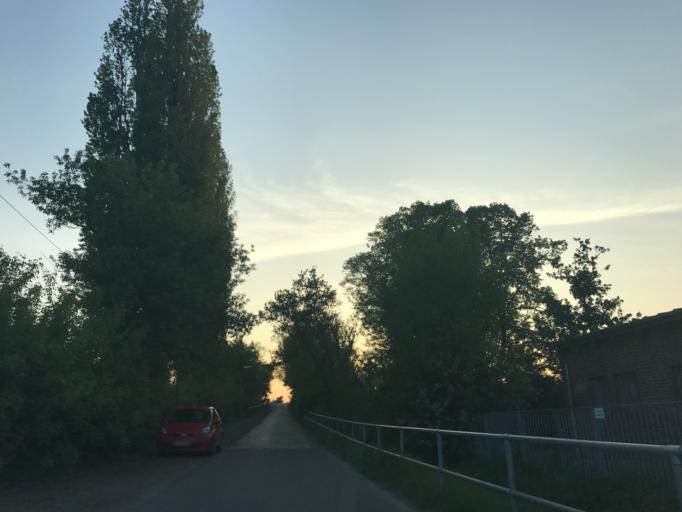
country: DE
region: Berlin
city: Staaken
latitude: 52.5378
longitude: 13.1450
